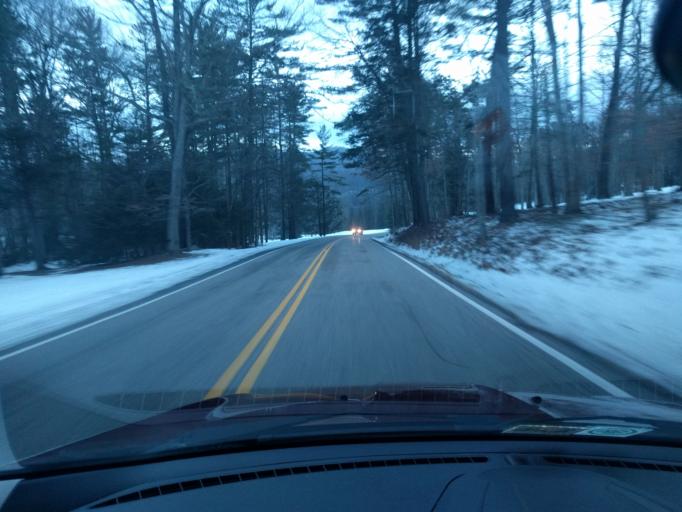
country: US
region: Virginia
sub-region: Bath County
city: Warm Springs
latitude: 37.9520
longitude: -79.8694
